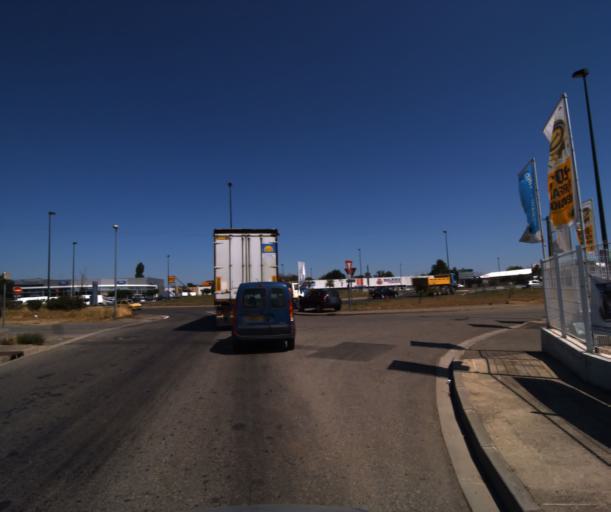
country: FR
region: Midi-Pyrenees
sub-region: Departement de la Haute-Garonne
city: Saubens
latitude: 43.4916
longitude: 1.3421
